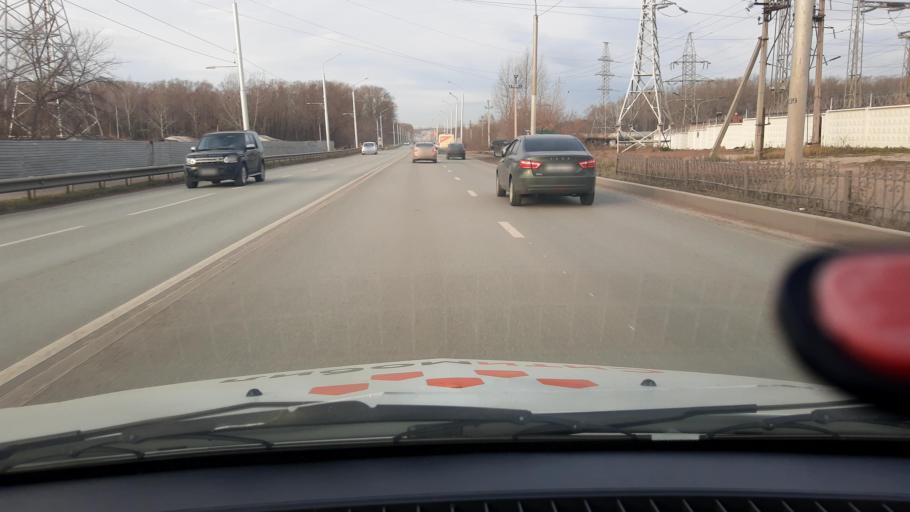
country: RU
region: Bashkortostan
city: Ufa
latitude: 54.7883
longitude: 56.1186
